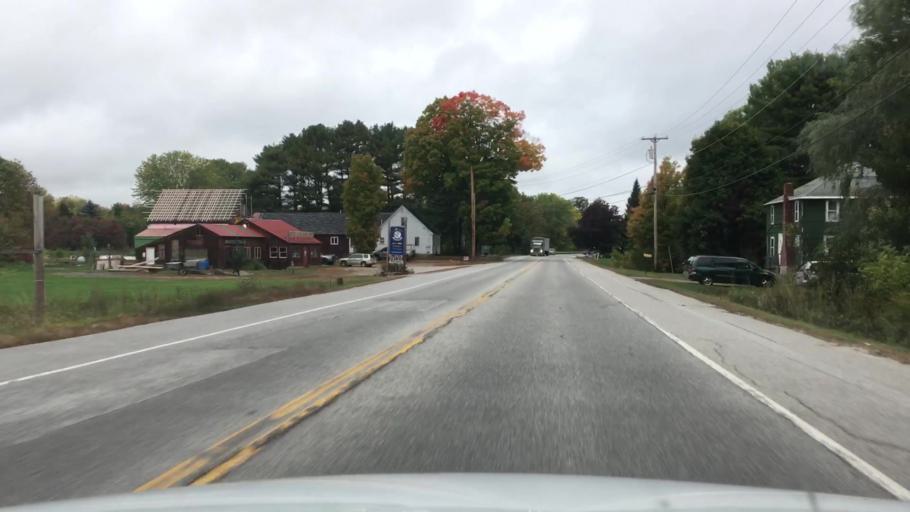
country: US
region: Maine
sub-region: Oxford County
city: Oxford
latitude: 44.1306
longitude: -70.4598
